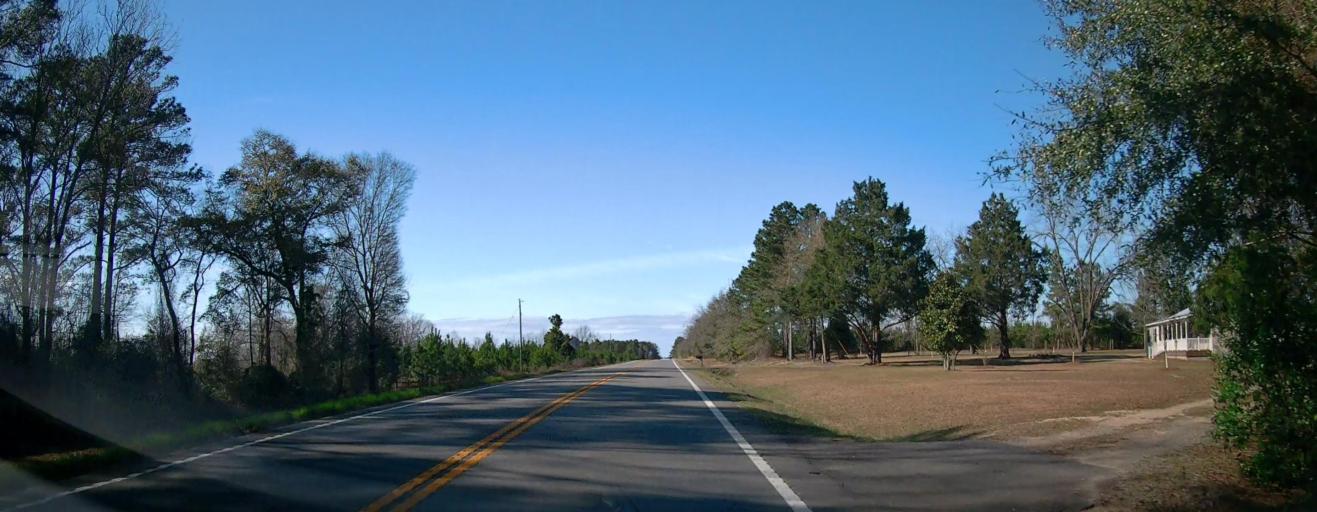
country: US
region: Georgia
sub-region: Macon County
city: Oglethorpe
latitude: 32.3536
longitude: -84.1736
